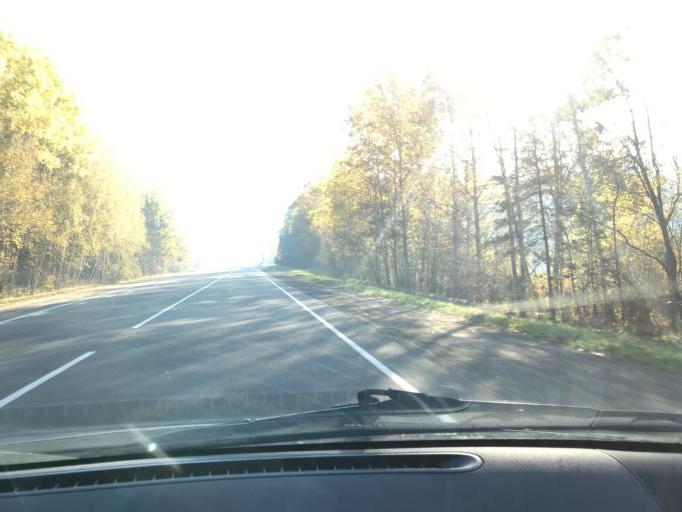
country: BY
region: Brest
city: Horad Luninyets
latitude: 52.2826
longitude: 26.8161
